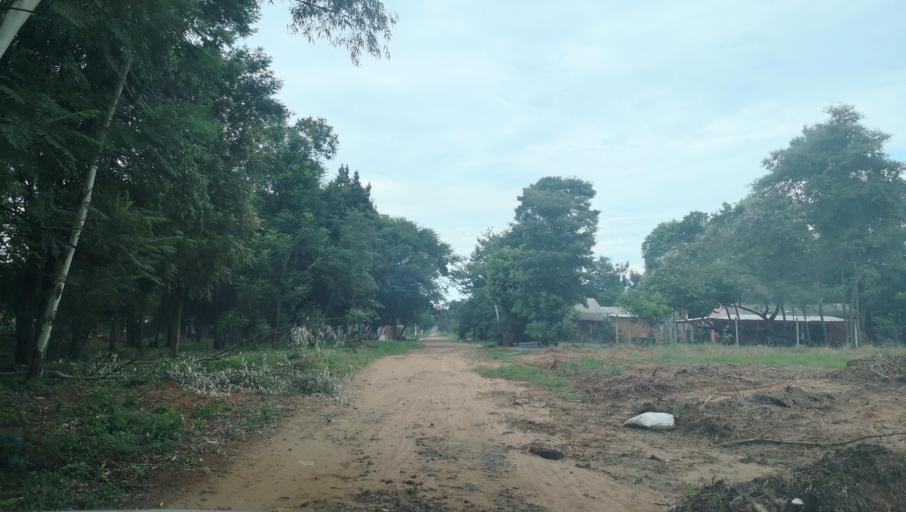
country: PY
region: San Pedro
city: Capiibary
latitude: -24.7375
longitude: -56.0246
